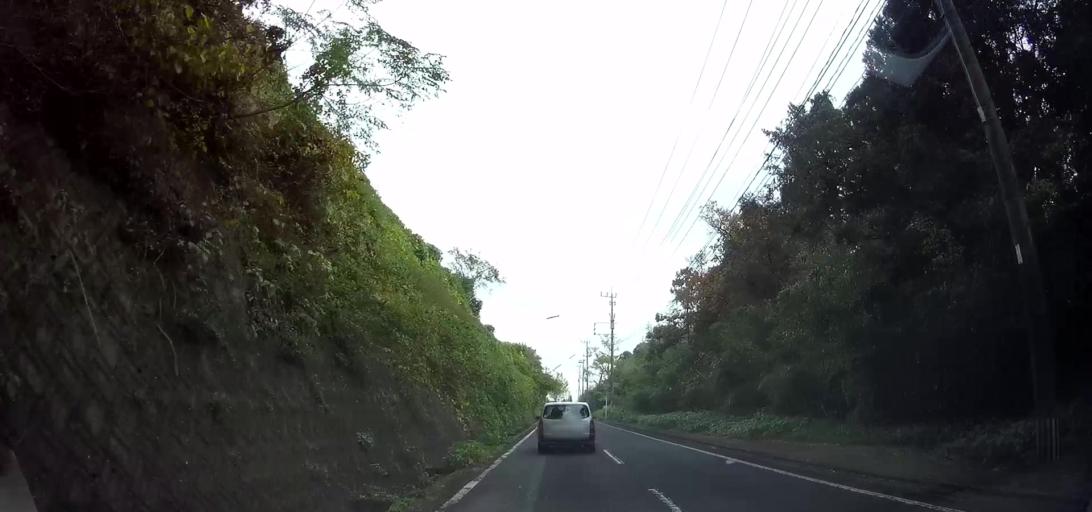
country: JP
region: Nagasaki
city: Shimabara
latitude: 32.6870
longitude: 130.2928
